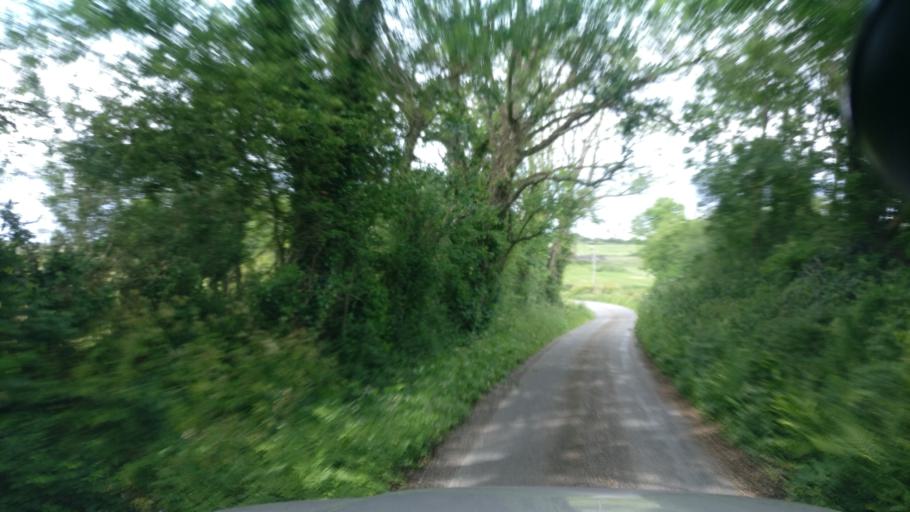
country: IE
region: Connaught
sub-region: County Galway
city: Ballinasloe
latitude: 53.2846
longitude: -8.3171
